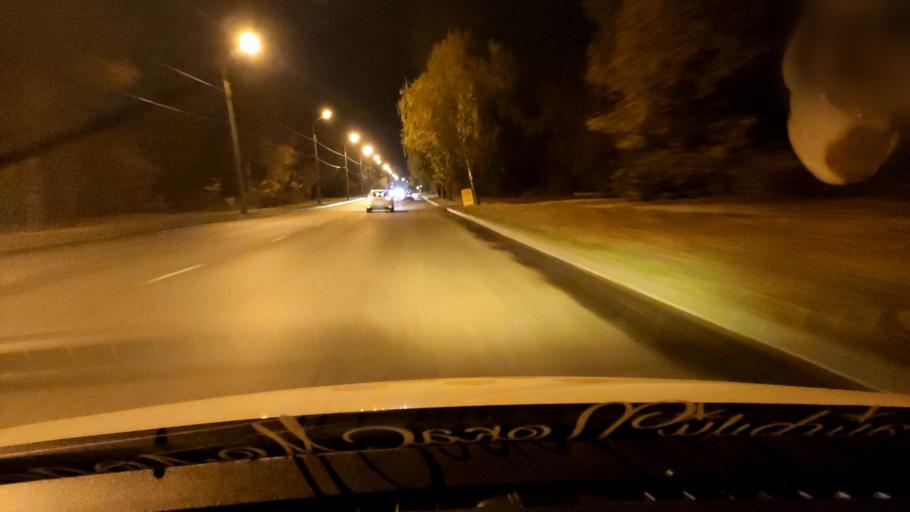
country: RU
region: Voronezj
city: Voronezh
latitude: 51.6449
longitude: 39.2109
